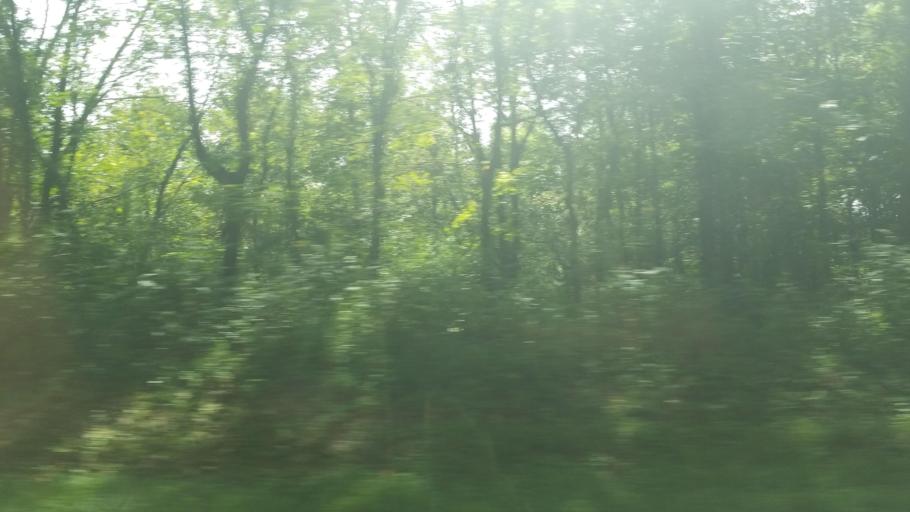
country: US
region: Illinois
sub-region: Saline County
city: Carrier Mills
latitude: 37.7990
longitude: -88.7390
